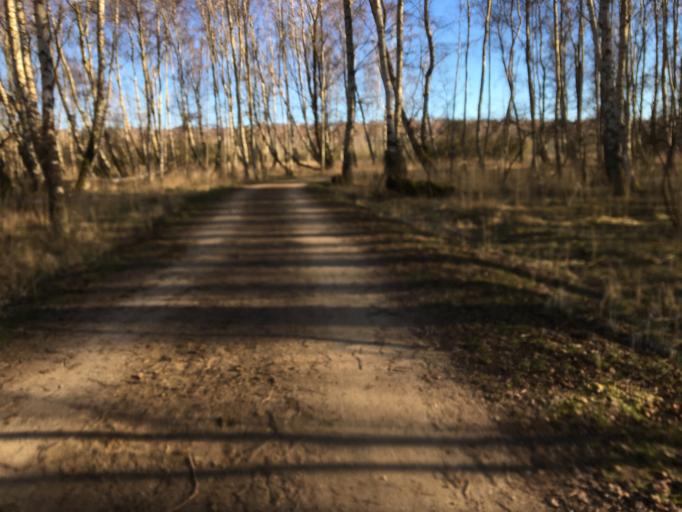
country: DK
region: Capital Region
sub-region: Tarnby Kommune
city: Tarnby
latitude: 55.5933
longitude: 12.5561
